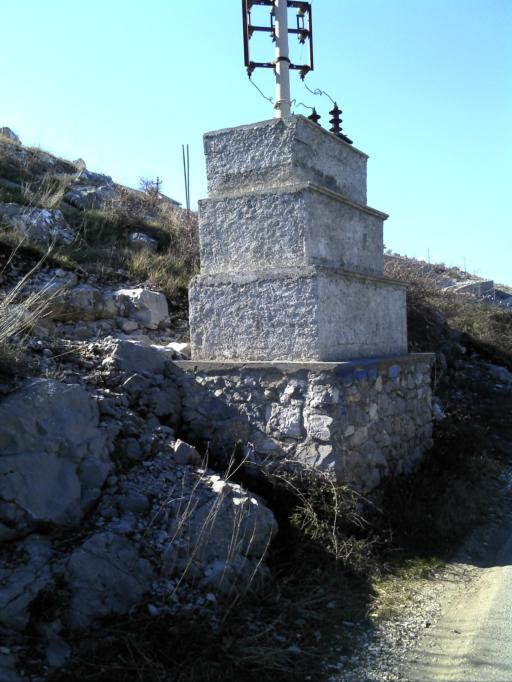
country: AL
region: Shkoder
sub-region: Rrethi i Shkodres
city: Berdica e Madhe
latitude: 42.0668
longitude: 19.4285
